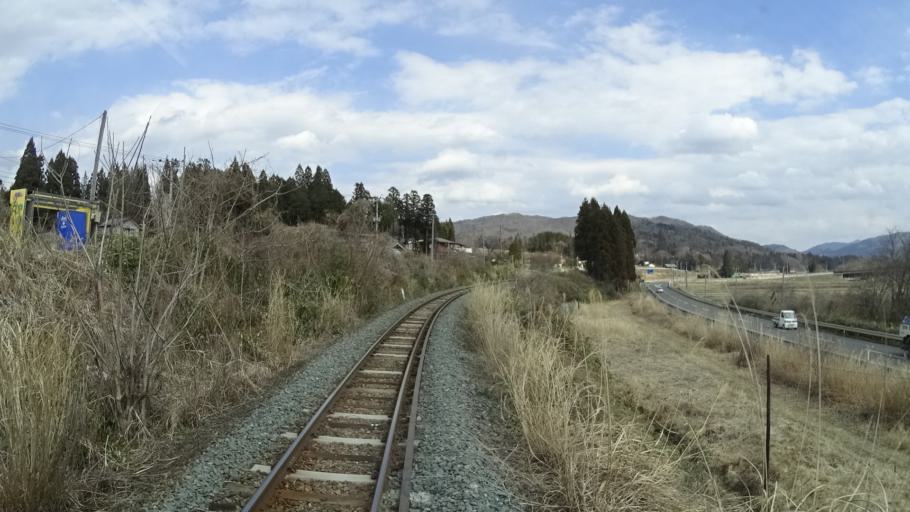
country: JP
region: Iwate
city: Hanamaki
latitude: 39.3779
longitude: 141.2450
